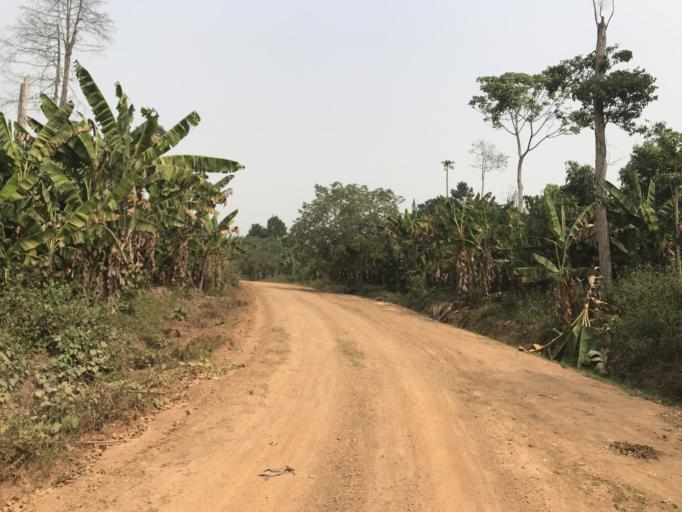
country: NG
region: Osun
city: Ifetedo
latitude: 7.0268
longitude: 4.4474
